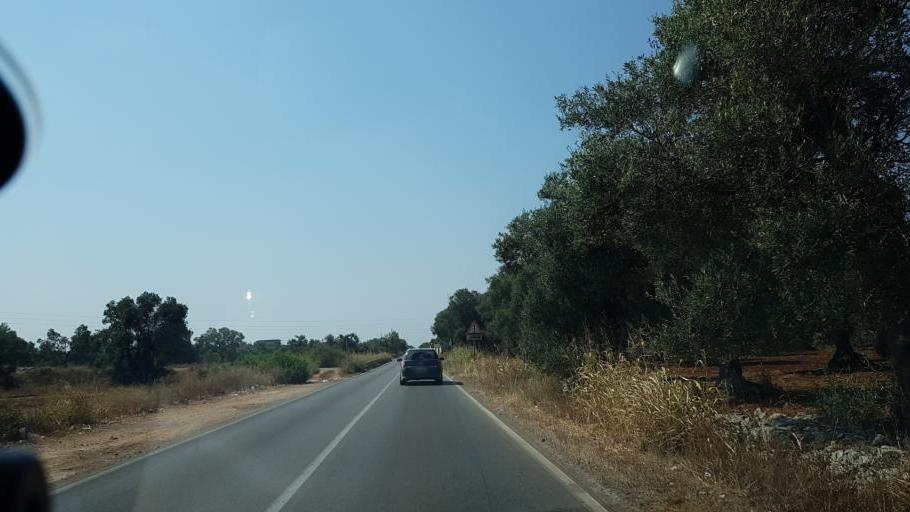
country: IT
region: Apulia
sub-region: Provincia di Taranto
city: Manduria
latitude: 40.4224
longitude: 17.6329
